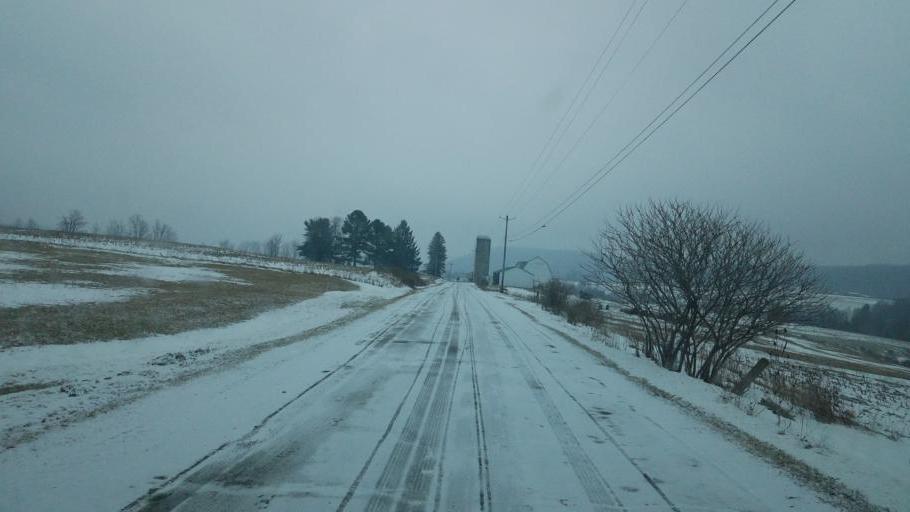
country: US
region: Pennsylvania
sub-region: Tioga County
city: Westfield
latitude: 42.1056
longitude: -77.4711
